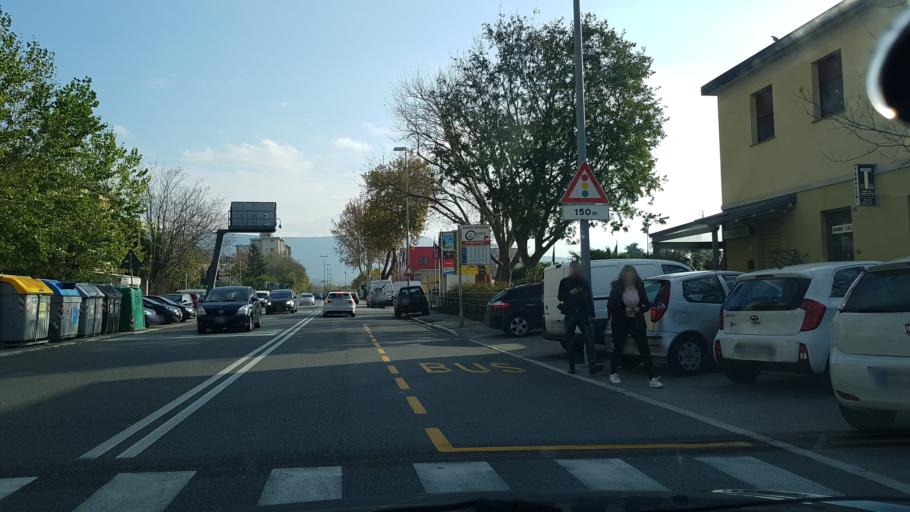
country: IT
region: Friuli Venezia Giulia
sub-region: Provincia di Trieste
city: Domio
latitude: 45.6203
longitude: 13.8098
